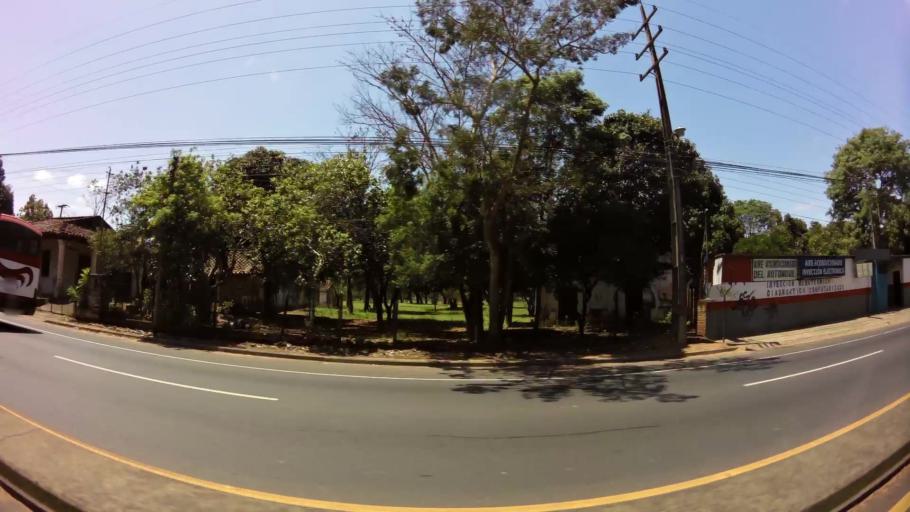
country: PY
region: Central
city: San Antonio
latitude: -25.4142
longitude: -57.5402
